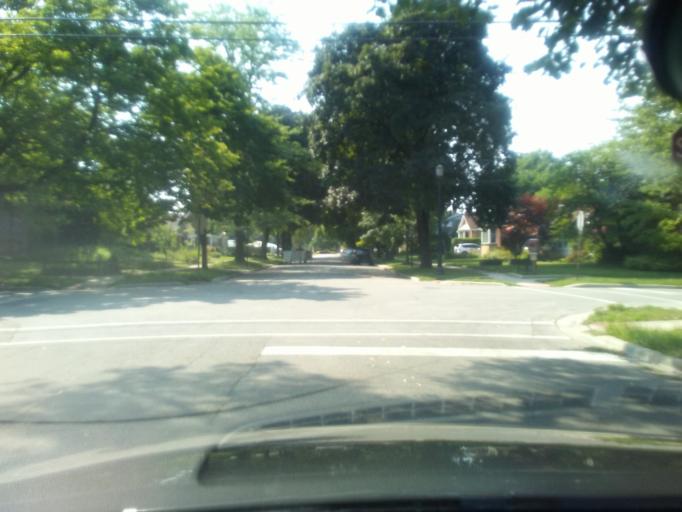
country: US
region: Illinois
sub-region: Cook County
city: Evanston
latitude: 42.0250
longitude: -87.6964
